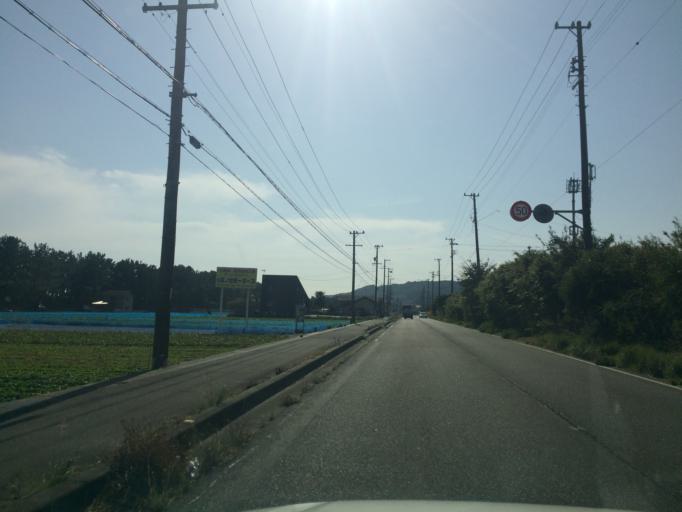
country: JP
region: Shizuoka
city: Sagara
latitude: 34.6710
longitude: 138.1962
